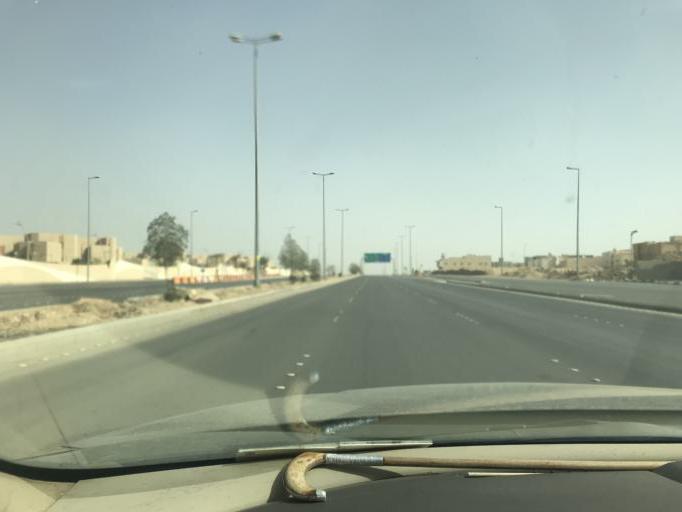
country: SA
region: Ar Riyad
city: Riyadh
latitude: 24.8260
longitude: 46.6836
